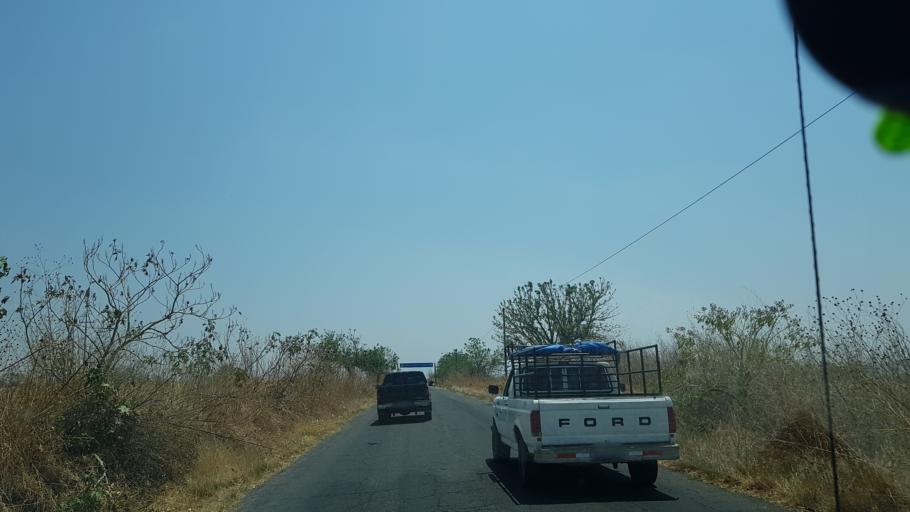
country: MX
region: Puebla
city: Tochimilco
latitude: 18.8871
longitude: -98.5445
